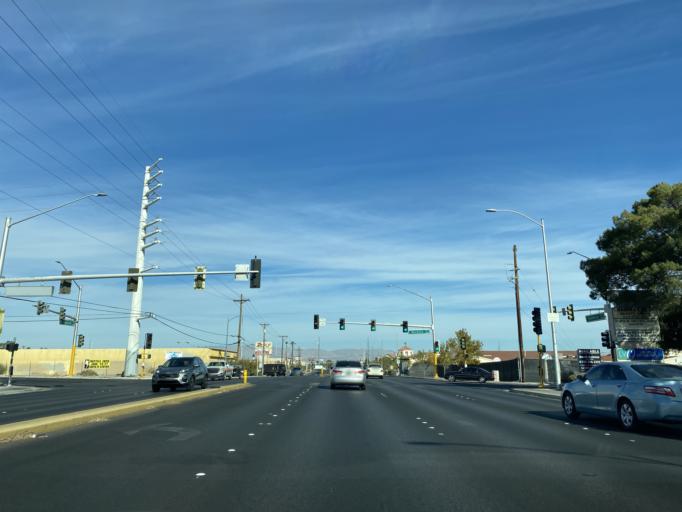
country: US
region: Nevada
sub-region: Clark County
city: Winchester
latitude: 36.1106
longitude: -115.1191
